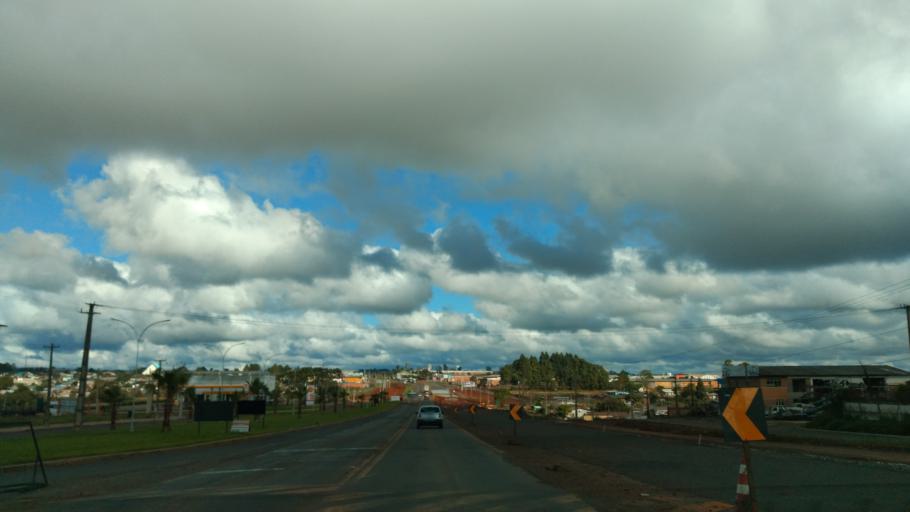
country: BR
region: Parana
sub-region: Guarapuava
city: Guarapuava
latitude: -25.3509
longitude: -51.4867
